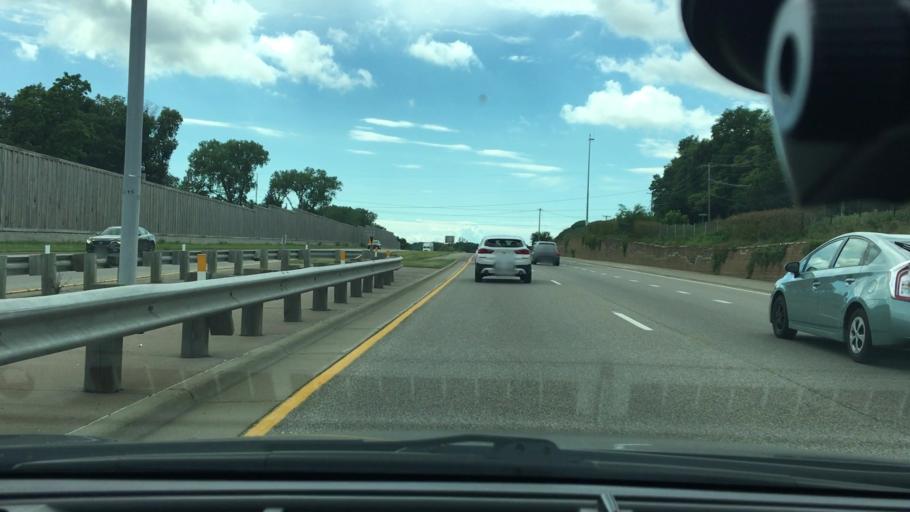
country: US
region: Minnesota
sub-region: Hennepin County
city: Golden Valley
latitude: 44.9847
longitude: -93.3524
